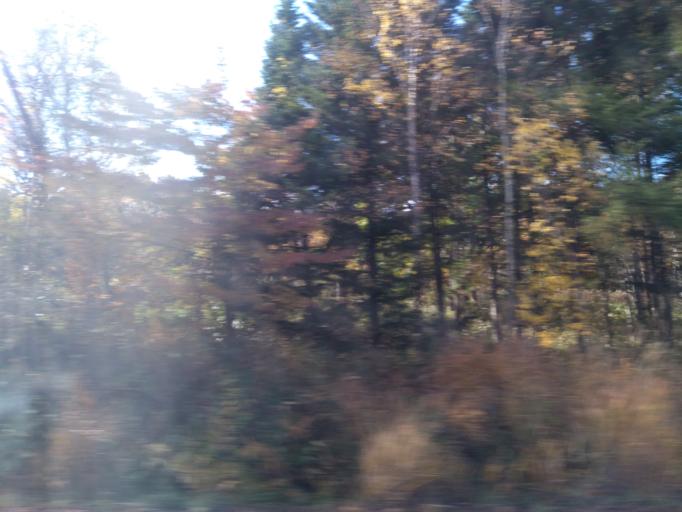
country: JP
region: Hokkaido
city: Kitahiroshima
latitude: 42.9356
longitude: 141.5723
